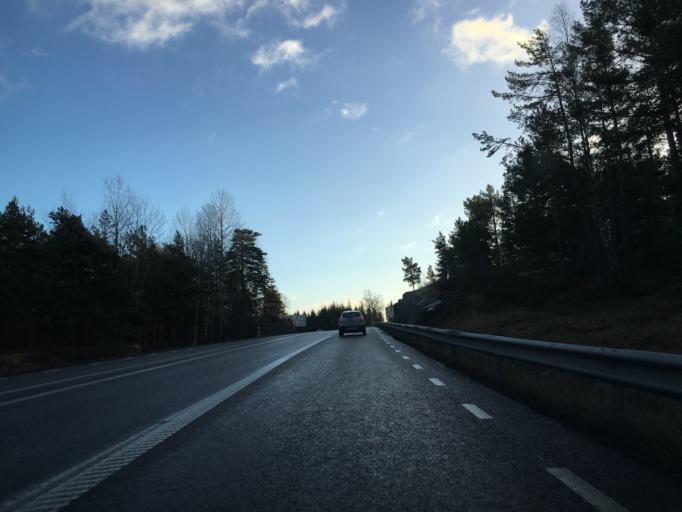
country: SE
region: Kalmar
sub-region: Vasterviks Kommun
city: Ankarsrum
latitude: 57.7220
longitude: 16.4574
